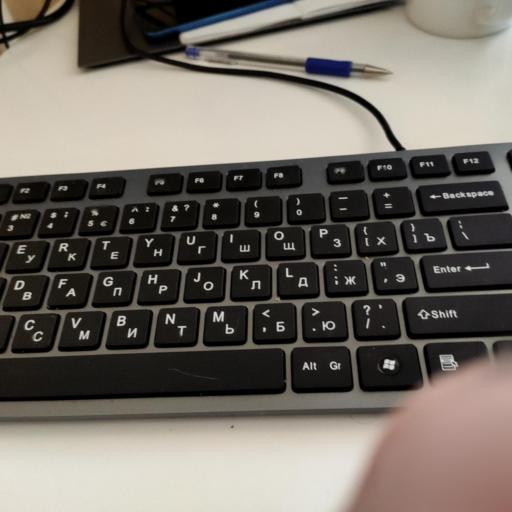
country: RU
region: Moskovskaya
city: Konstantinovo
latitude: 56.6339
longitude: 38.0113
